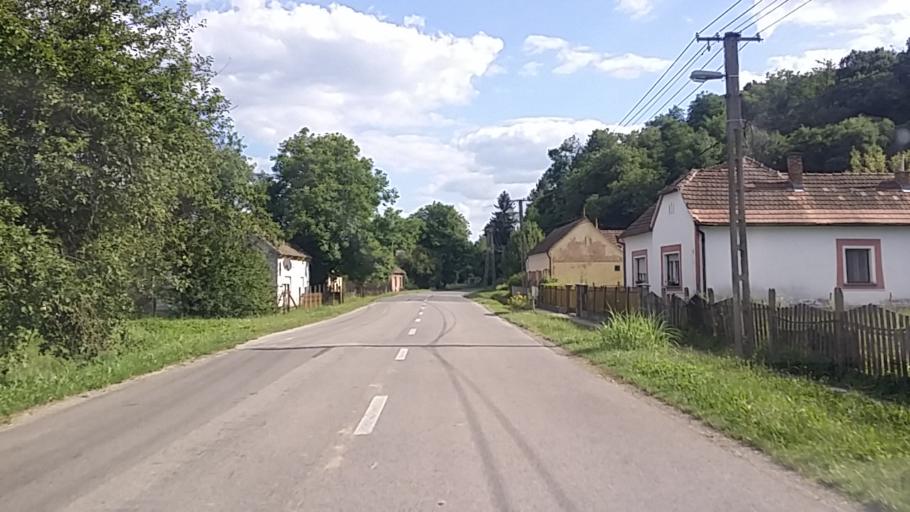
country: HU
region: Baranya
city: Sasd
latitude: 46.1975
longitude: 18.0825
